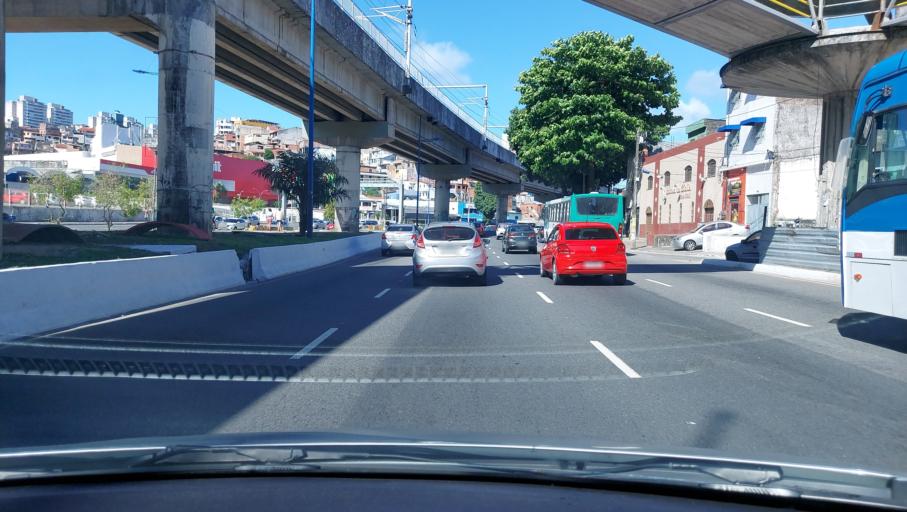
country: BR
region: Bahia
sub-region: Salvador
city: Salvador
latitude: -12.9841
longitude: -38.4884
